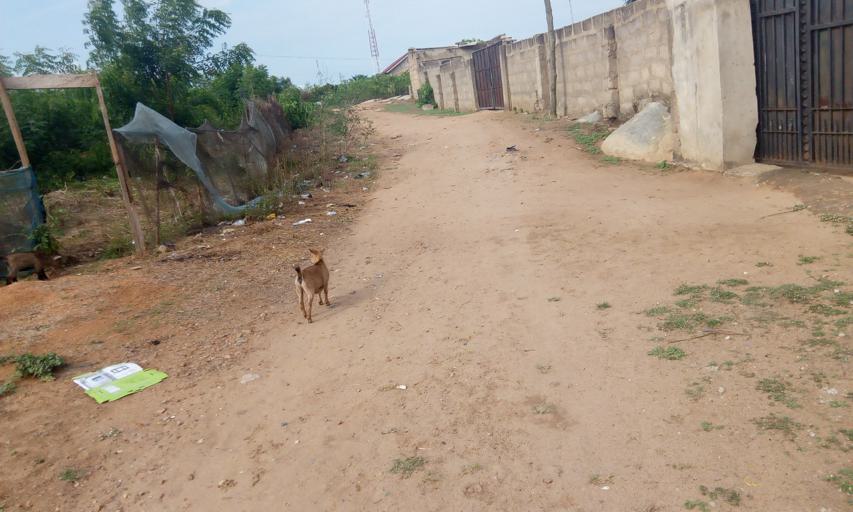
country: GH
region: Central
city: Winneba
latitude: 5.3581
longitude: -0.6230
